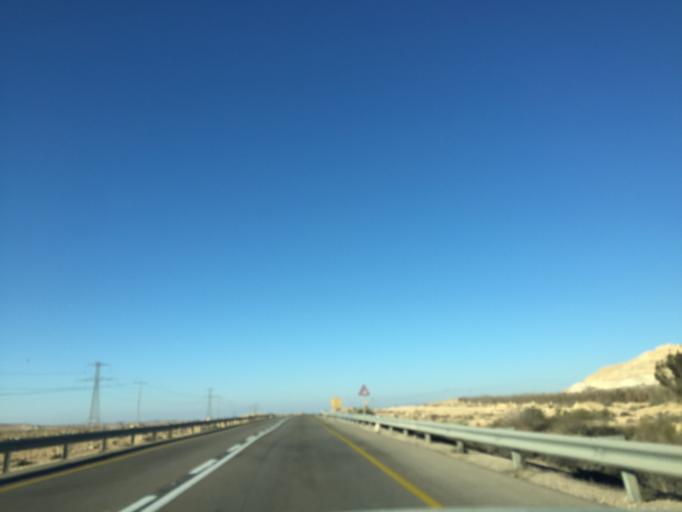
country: IL
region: Southern District
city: Midreshet Ben-Gurion
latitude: 30.7854
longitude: 34.7683
